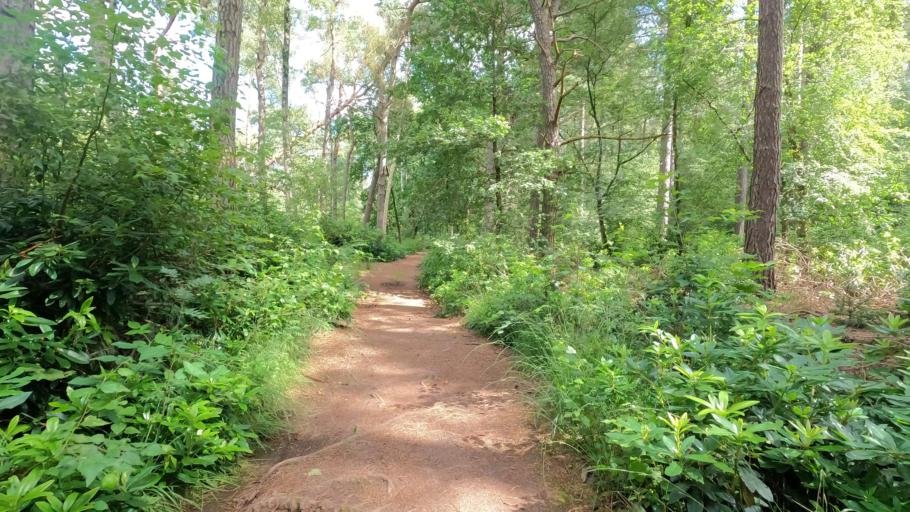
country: BE
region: Flanders
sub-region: Provincie Antwerpen
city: Zoersel
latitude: 51.2568
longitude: 4.7496
